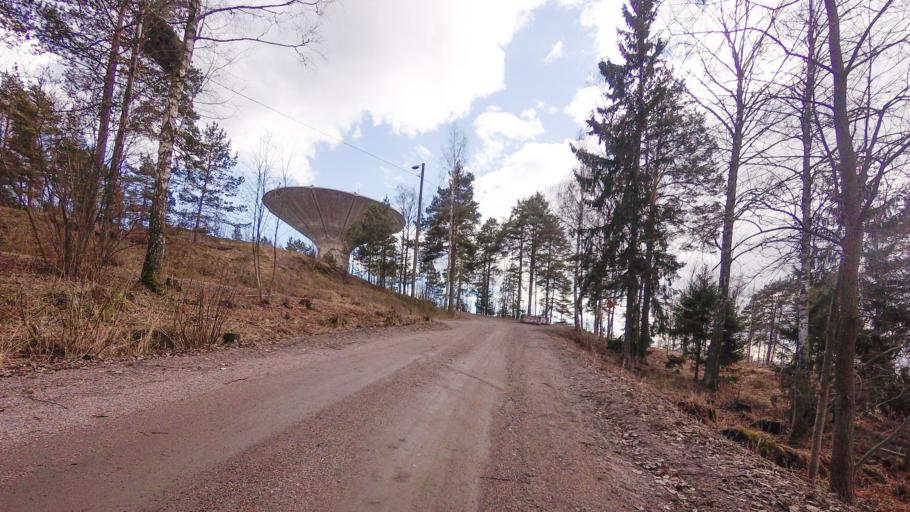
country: FI
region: Uusimaa
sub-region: Helsinki
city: Vantaa
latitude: 60.1992
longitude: 25.0492
